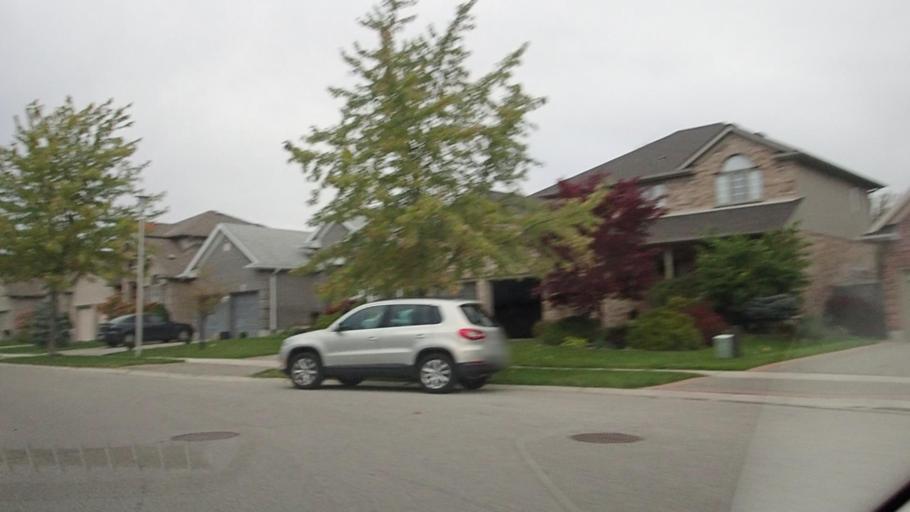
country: CA
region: Ontario
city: London
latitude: 43.0399
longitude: -81.2717
